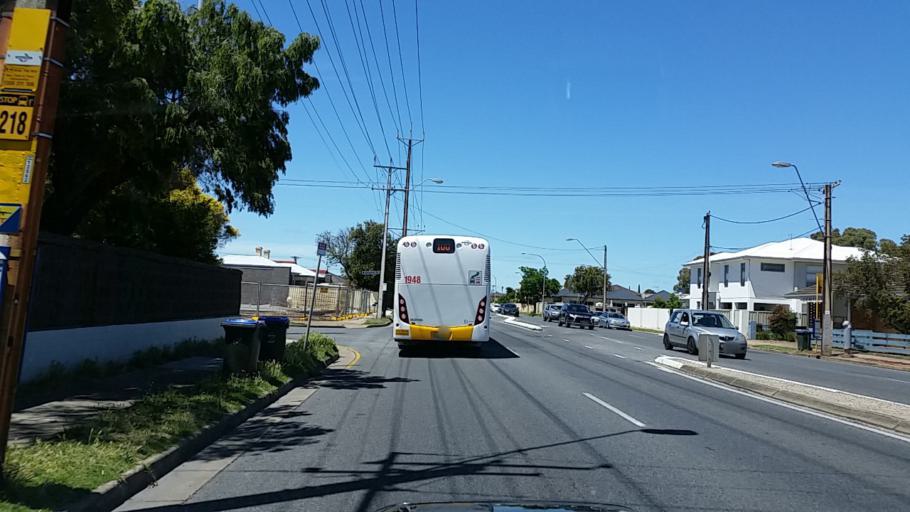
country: AU
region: South Australia
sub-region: Charles Sturt
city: Woodville West
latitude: -34.8860
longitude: 138.5313
